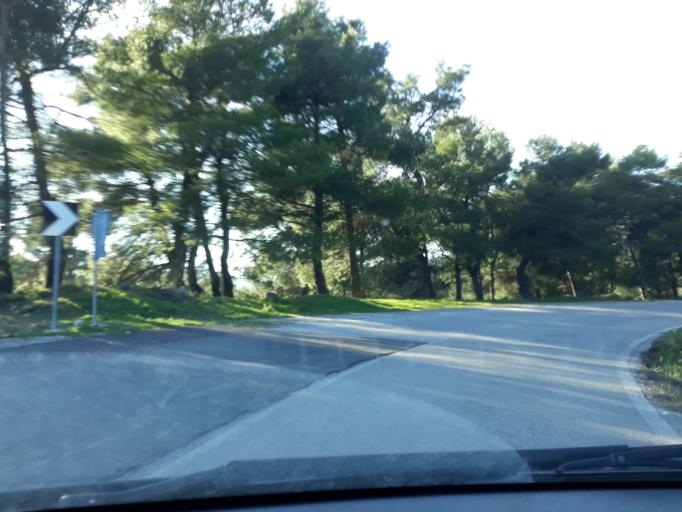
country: GR
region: Attica
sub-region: Nomarchia Dytikis Attikis
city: Fyli
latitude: 38.1490
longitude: 23.6330
